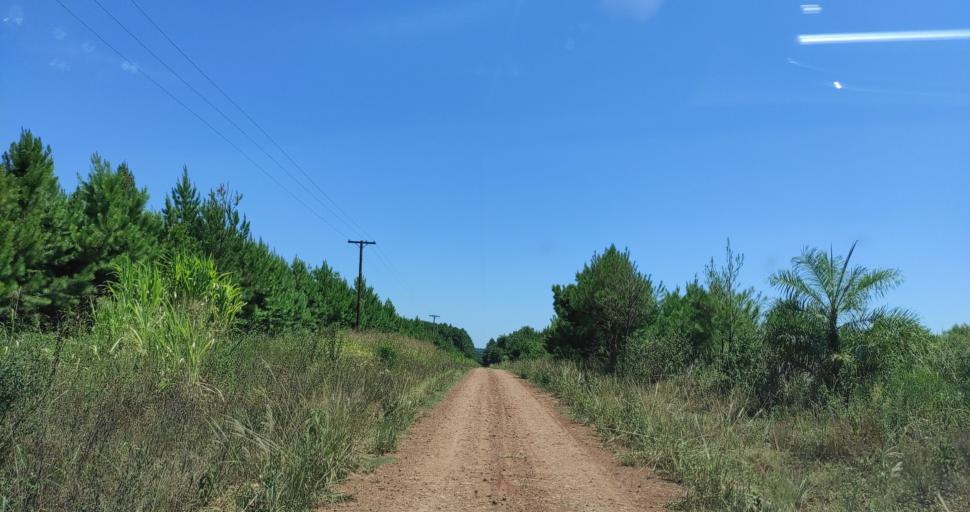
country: AR
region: Misiones
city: Capiovi
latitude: -26.9315
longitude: -55.0967
